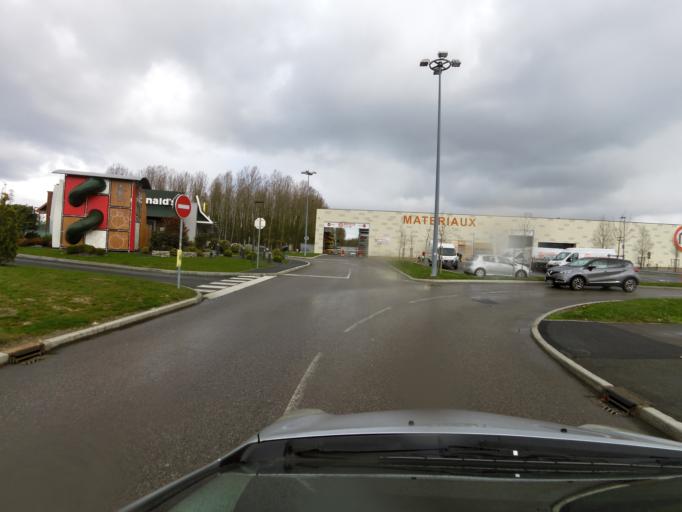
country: FR
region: Picardie
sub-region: Departement de l'Oise
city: Les Ageux
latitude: 49.3185
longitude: 2.6055
